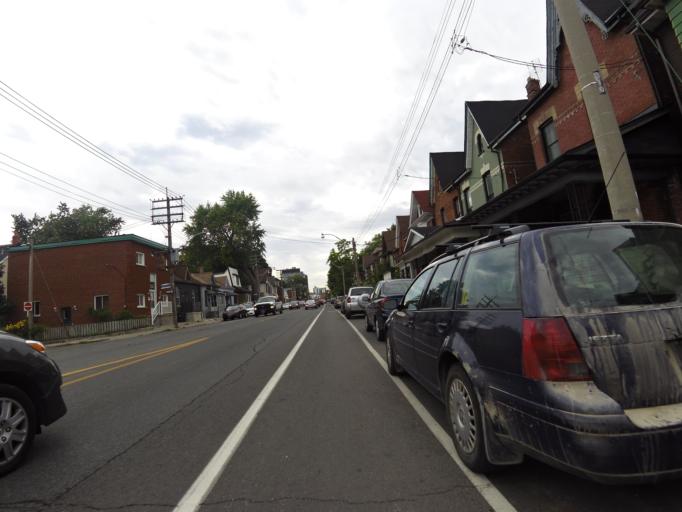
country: CA
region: Ontario
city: Toronto
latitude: 43.6659
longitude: -79.3373
